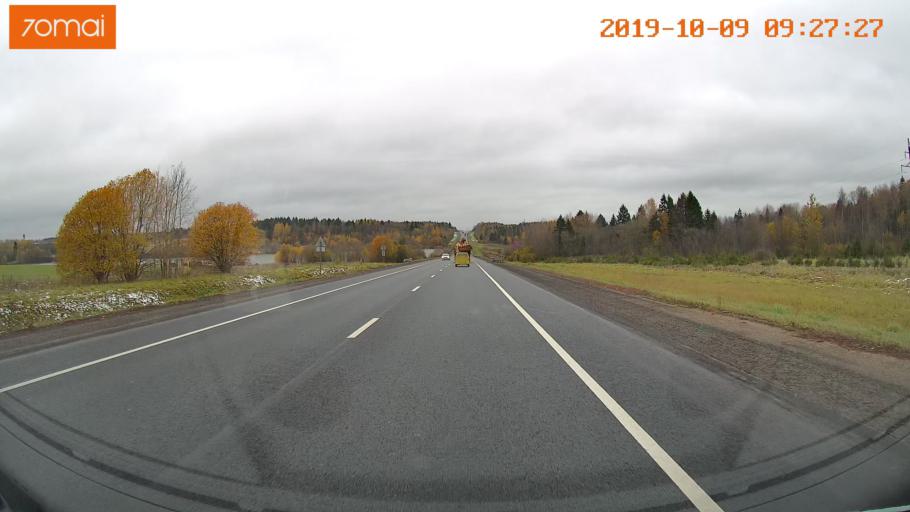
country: RU
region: Vologda
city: Vologda
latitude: 59.1129
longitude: 39.9783
